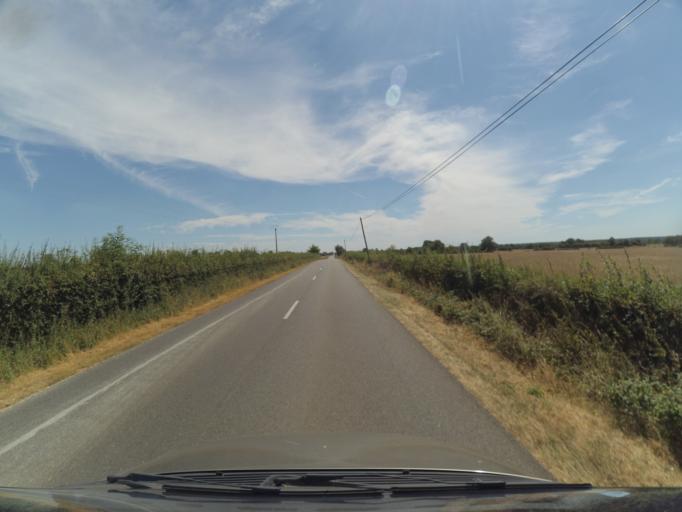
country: FR
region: Poitou-Charentes
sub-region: Departement de la Vienne
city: Usson-du-Poitou
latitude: 46.1705
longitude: 0.5465
